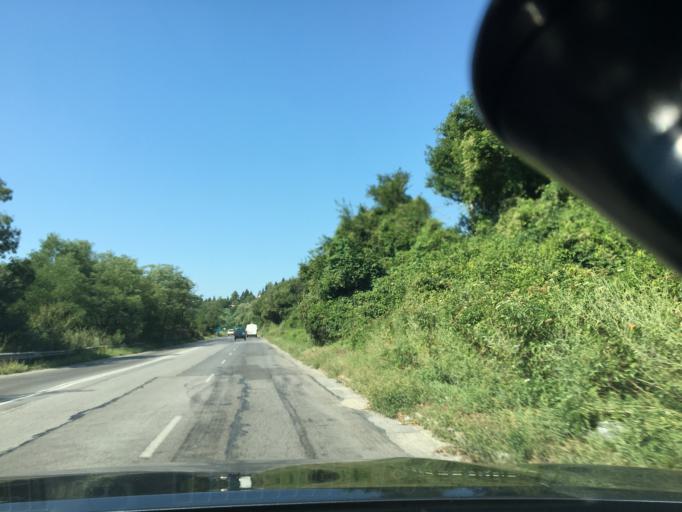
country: BG
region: Sofiya
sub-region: Obshtina Bozhurishte
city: Bozhurishte
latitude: 42.6348
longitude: 23.1939
